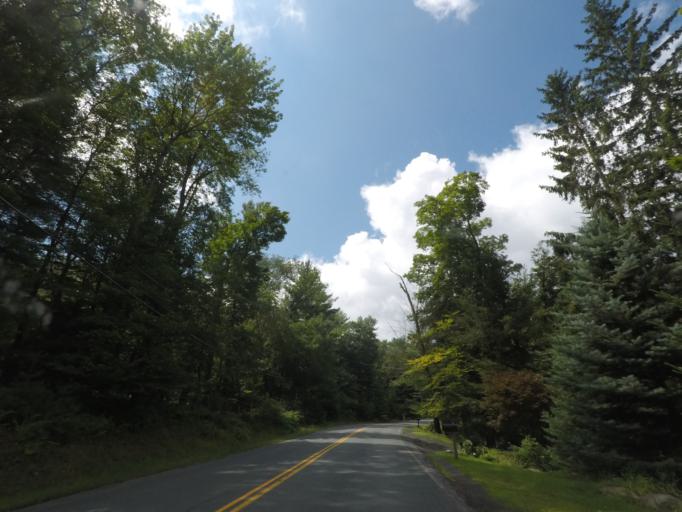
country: US
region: New York
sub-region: Rensselaer County
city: Averill Park
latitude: 42.6454
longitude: -73.4869
